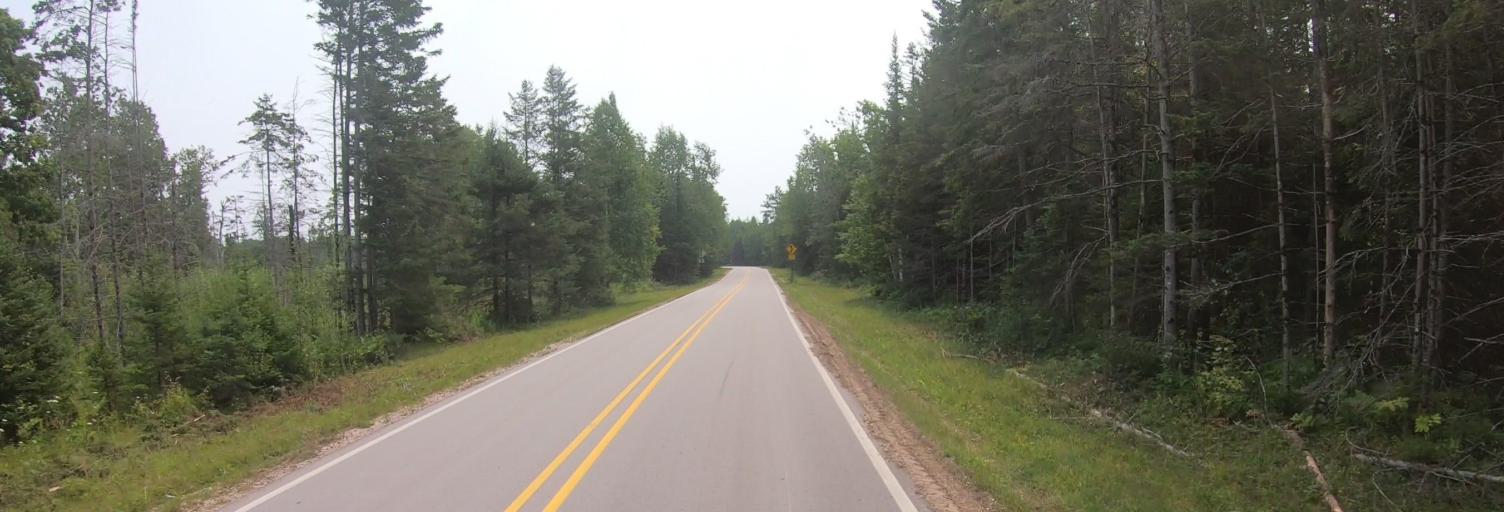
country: CA
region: Ontario
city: Thessalon
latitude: 45.9483
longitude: -83.6006
